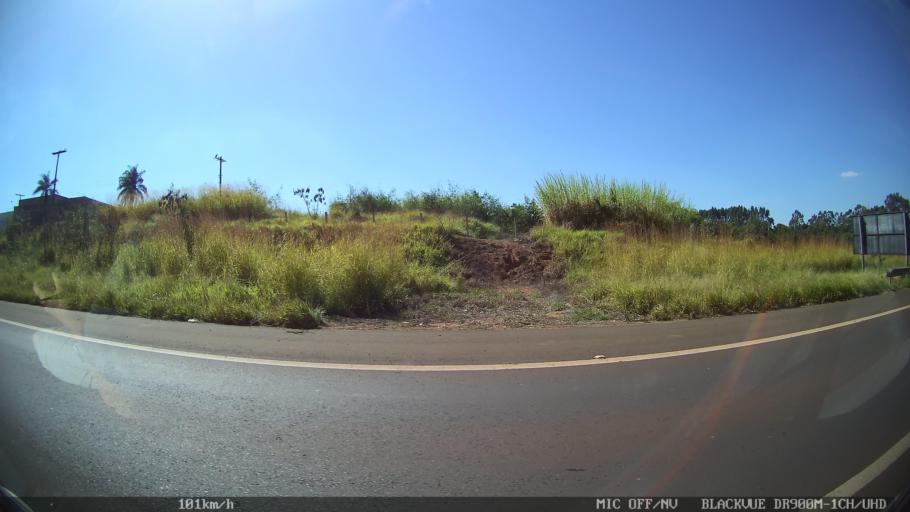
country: BR
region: Sao Paulo
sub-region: Franca
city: Franca
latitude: -20.5504
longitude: -47.4536
